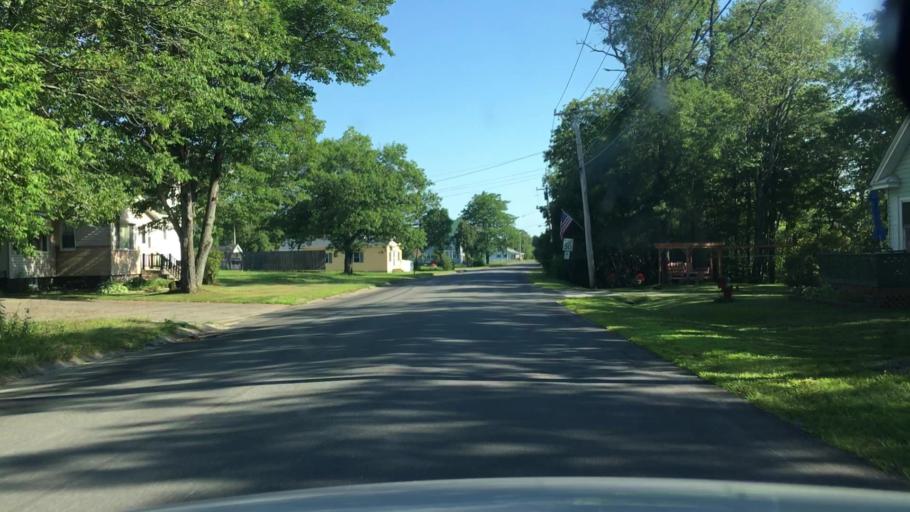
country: US
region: Maine
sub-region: Penobscot County
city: Howland
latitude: 45.2365
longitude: -68.6492
